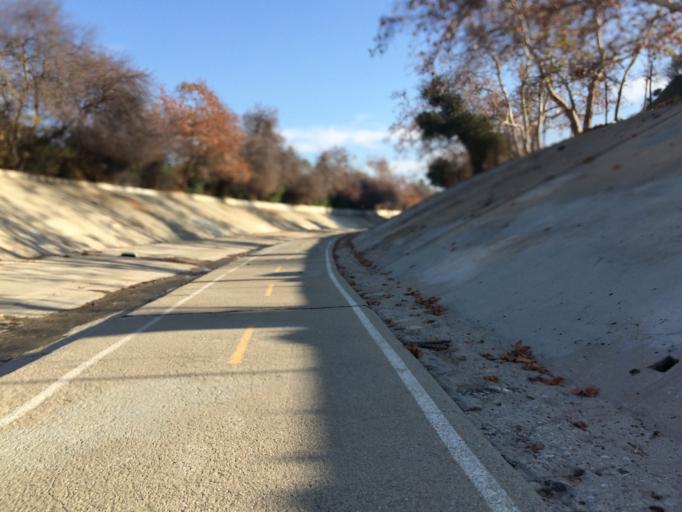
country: US
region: California
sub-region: Los Angeles County
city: South Pasadena
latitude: 34.1011
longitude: -118.2005
